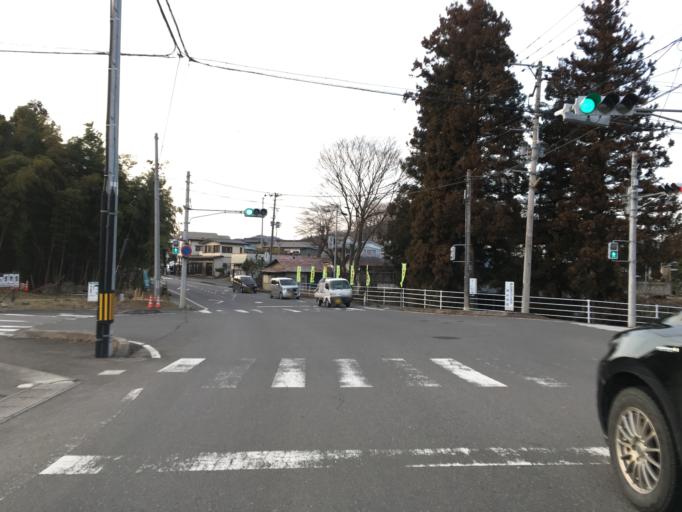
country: JP
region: Ibaraki
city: Daigo
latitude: 36.9528
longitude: 140.4063
